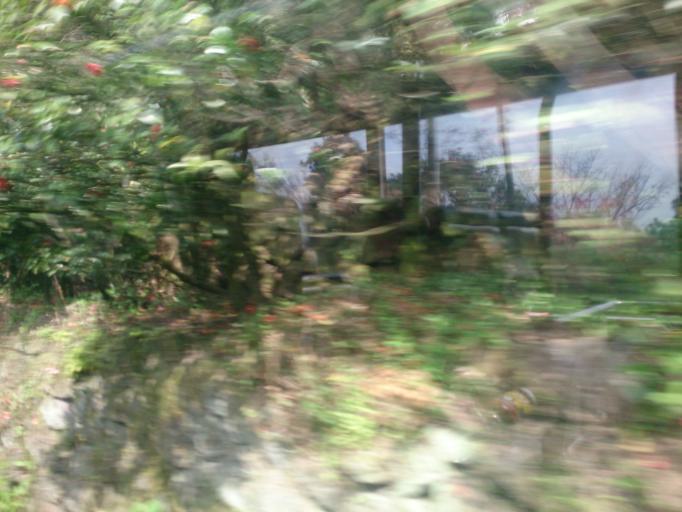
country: TW
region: Taipei
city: Taipei
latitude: 25.1650
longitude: 121.5437
